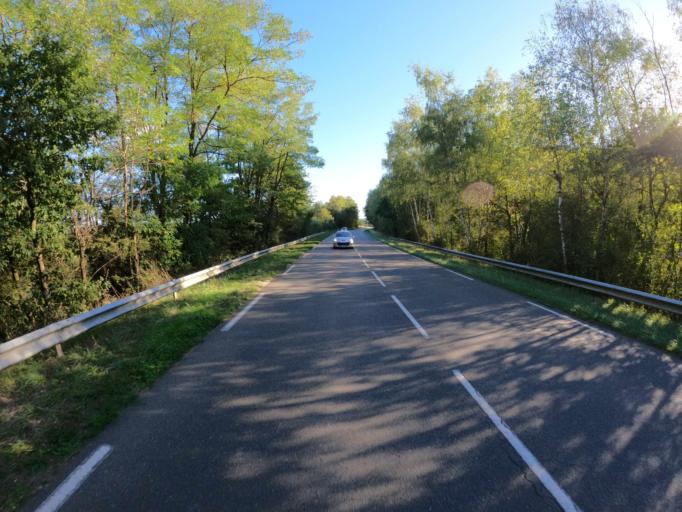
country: FR
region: Bourgogne
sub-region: Departement de Saone-et-Loire
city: Montchanin
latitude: 46.7403
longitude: 4.4452
